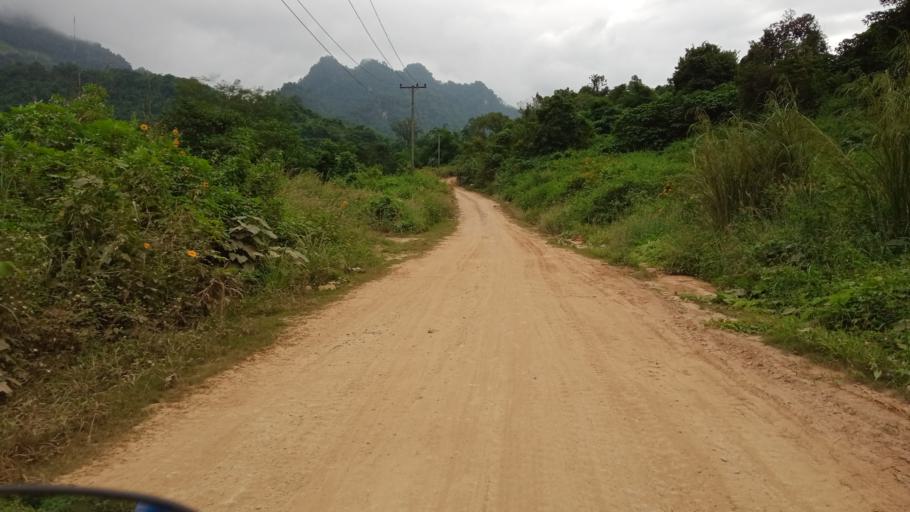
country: LA
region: Xiangkhoang
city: Phonsavan
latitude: 19.0946
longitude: 102.9885
